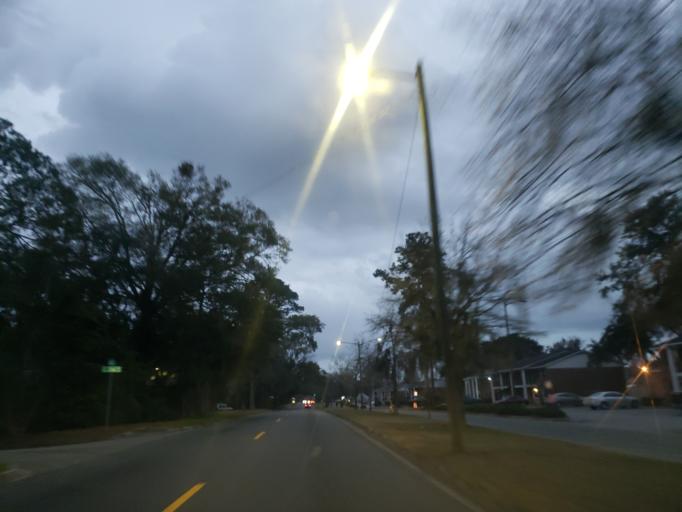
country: US
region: Georgia
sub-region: Chatham County
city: Thunderbolt
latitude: 32.0525
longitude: -81.0667
